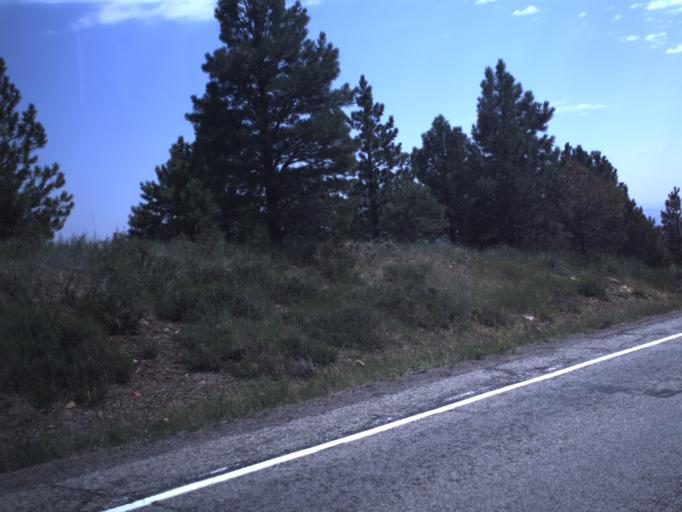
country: US
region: Utah
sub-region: Daggett County
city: Manila
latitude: 40.8720
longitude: -109.4960
